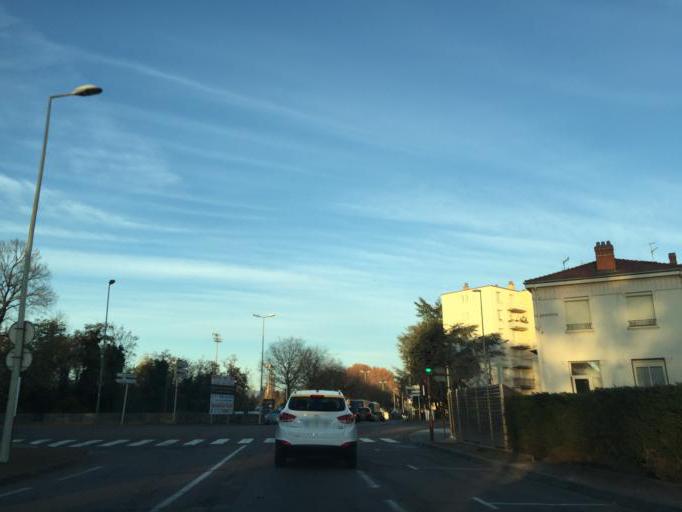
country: FR
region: Rhone-Alpes
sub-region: Departement de la Loire
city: Roanne
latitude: 46.0324
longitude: 4.0604
